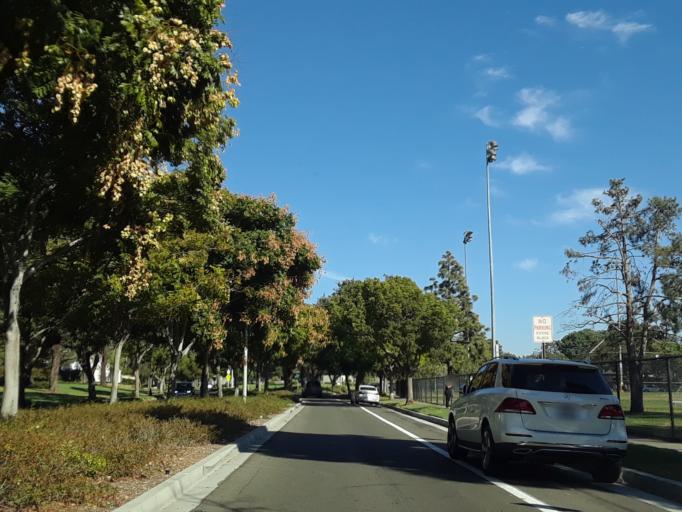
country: US
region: California
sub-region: Orange County
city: Irvine
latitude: 33.6631
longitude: -117.8192
